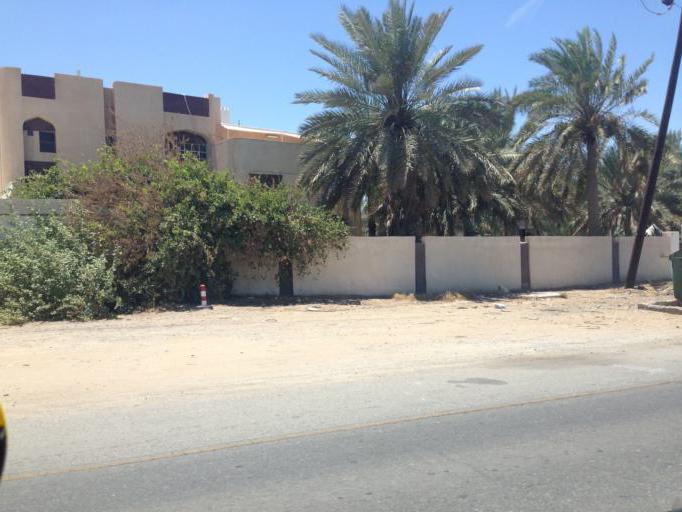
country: OM
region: Muhafazat Masqat
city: As Sib al Jadidah
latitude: 23.6318
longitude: 58.2477
